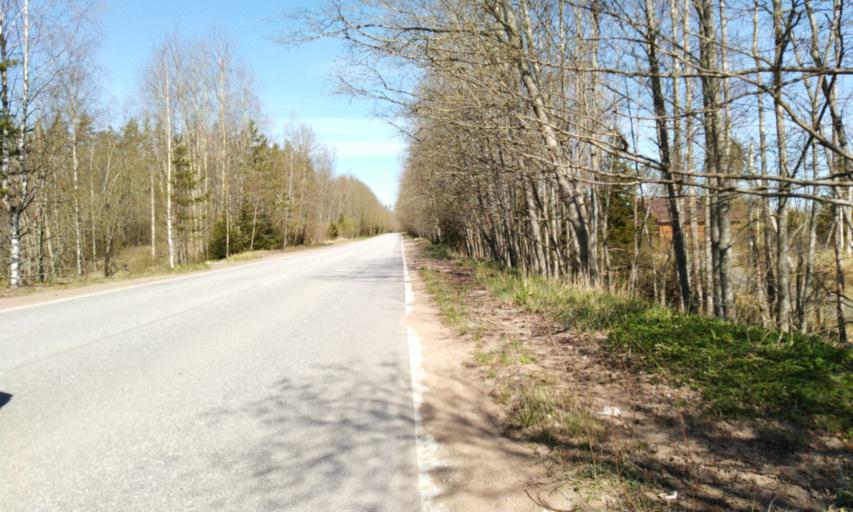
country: RU
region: Leningrad
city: Garbolovo
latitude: 60.4056
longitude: 30.4678
